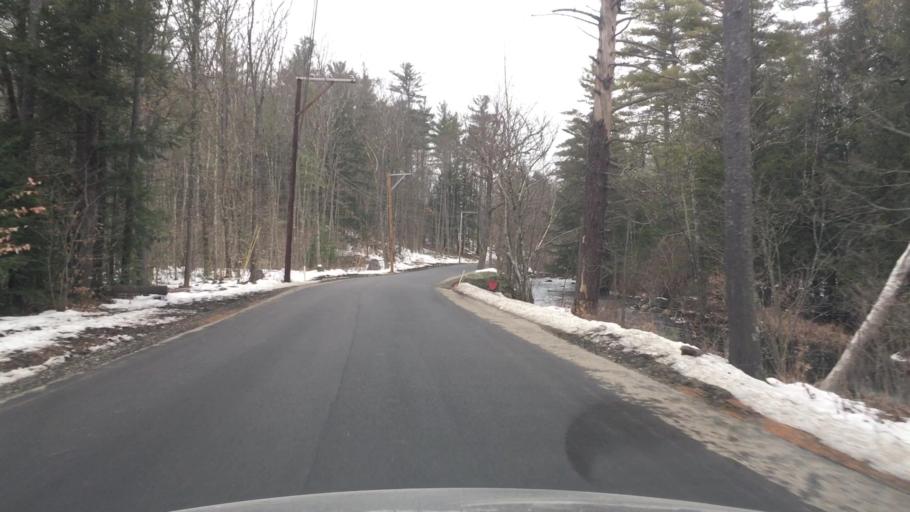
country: US
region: New Hampshire
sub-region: Hillsborough County
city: New Boston
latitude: 43.0027
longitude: -71.6627
